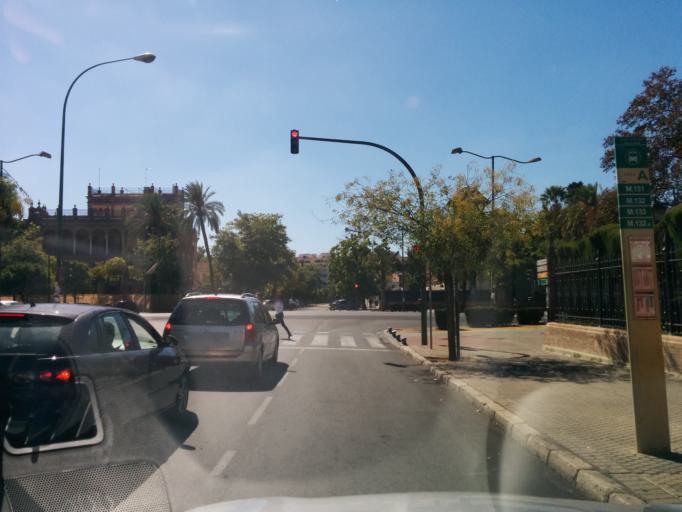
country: ES
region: Andalusia
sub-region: Provincia de Sevilla
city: Sevilla
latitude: 37.3604
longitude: -5.9818
